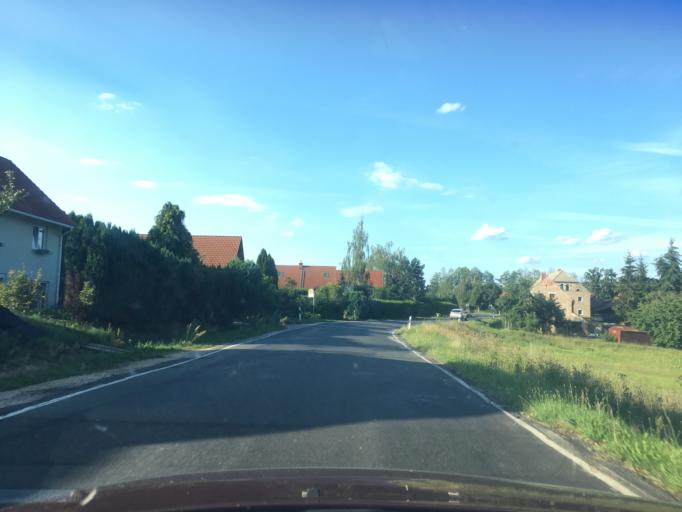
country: DE
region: Saxony
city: Goerlitz
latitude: 51.1982
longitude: 14.9978
